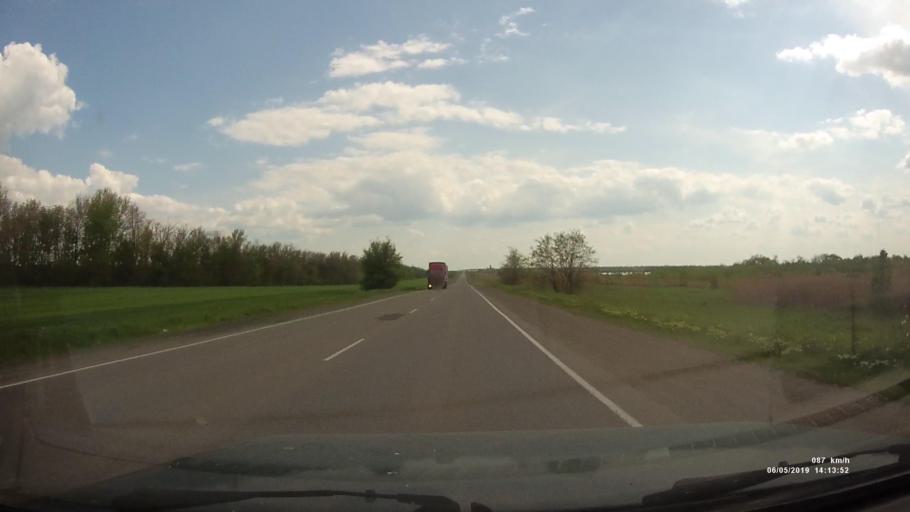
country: RU
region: Rostov
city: Kamenolomni
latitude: 47.6554
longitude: 40.2943
